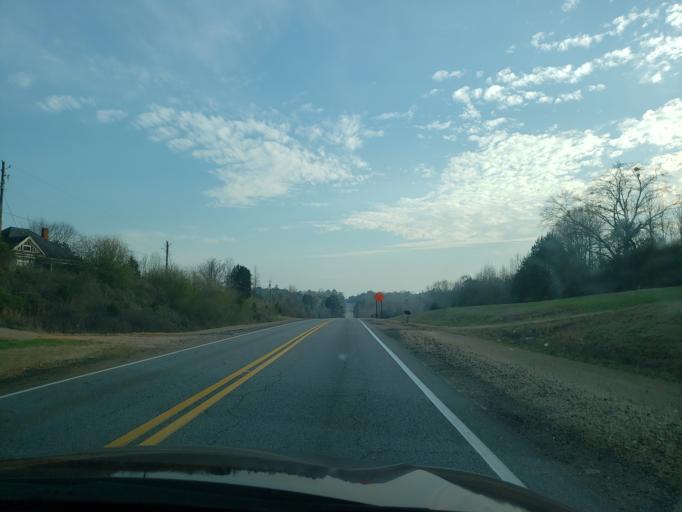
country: US
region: Alabama
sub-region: Hale County
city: Moundville
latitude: 32.9288
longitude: -87.6356
